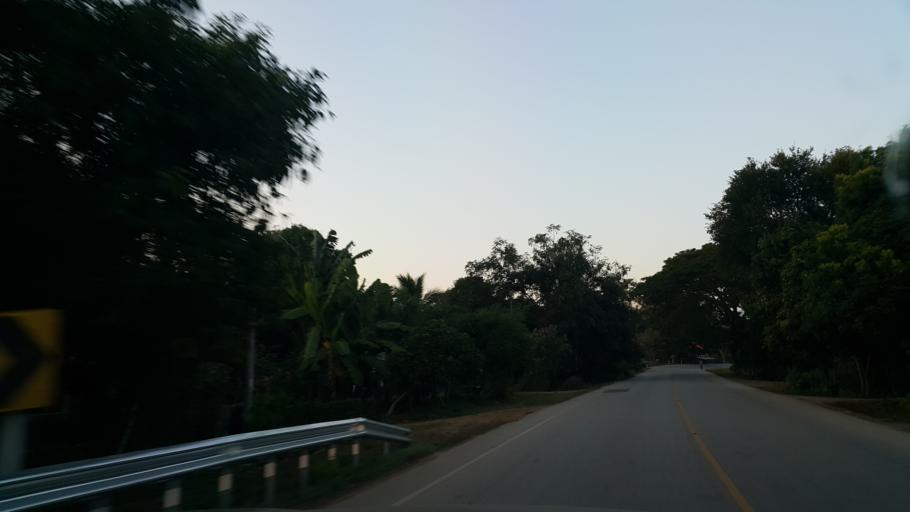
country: TH
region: Phrae
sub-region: Amphoe Wang Chin
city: Wang Chin
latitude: 17.8710
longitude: 99.6192
